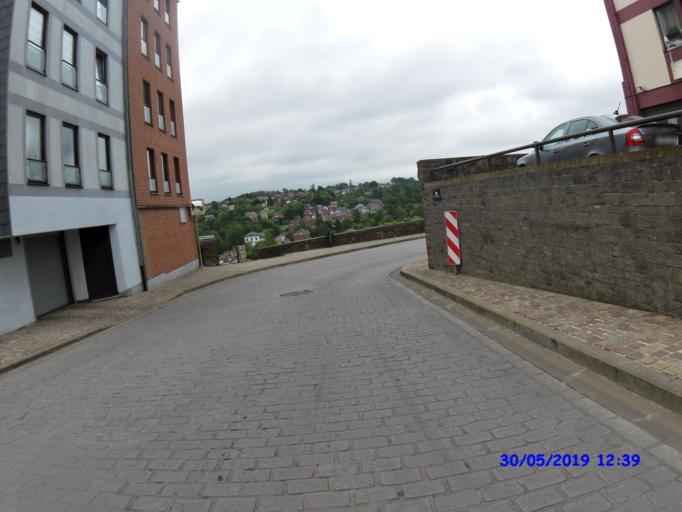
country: BE
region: Wallonia
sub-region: Province du Hainaut
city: Thuin
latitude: 50.3396
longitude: 4.2879
